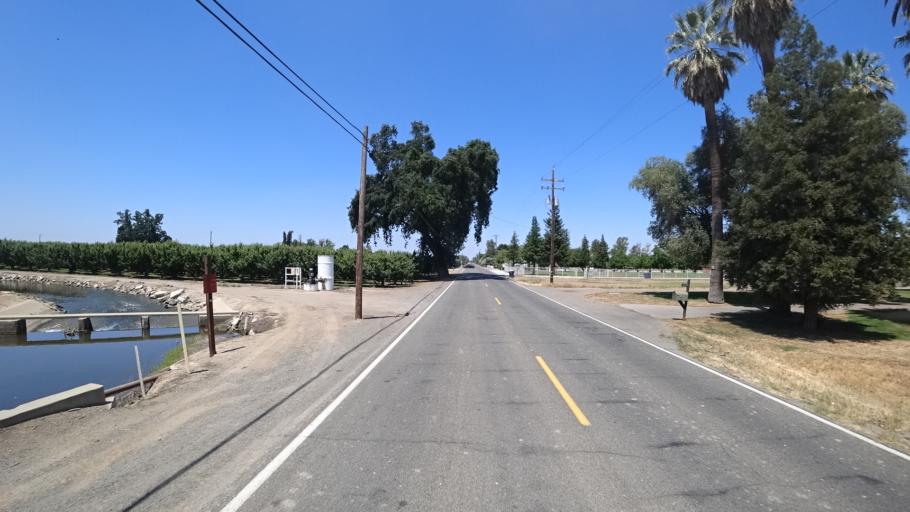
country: US
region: California
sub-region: Kings County
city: Lucerne
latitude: 36.3815
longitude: -119.6550
